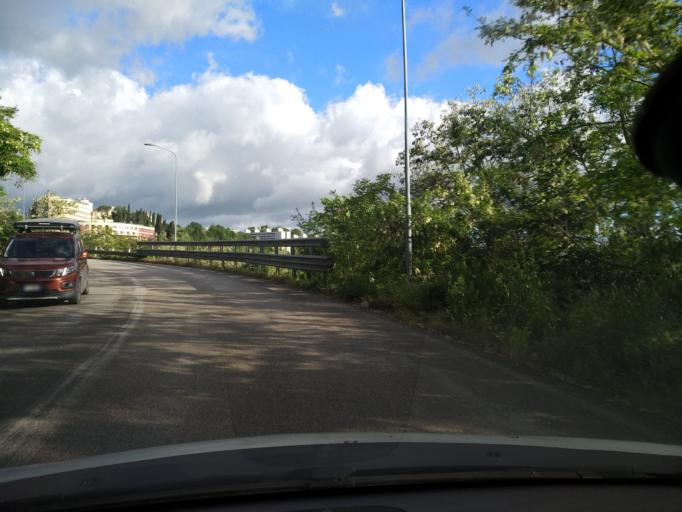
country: IT
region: The Marches
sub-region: Provincia di Pesaro e Urbino
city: Urbino
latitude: 43.7306
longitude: 12.6383
